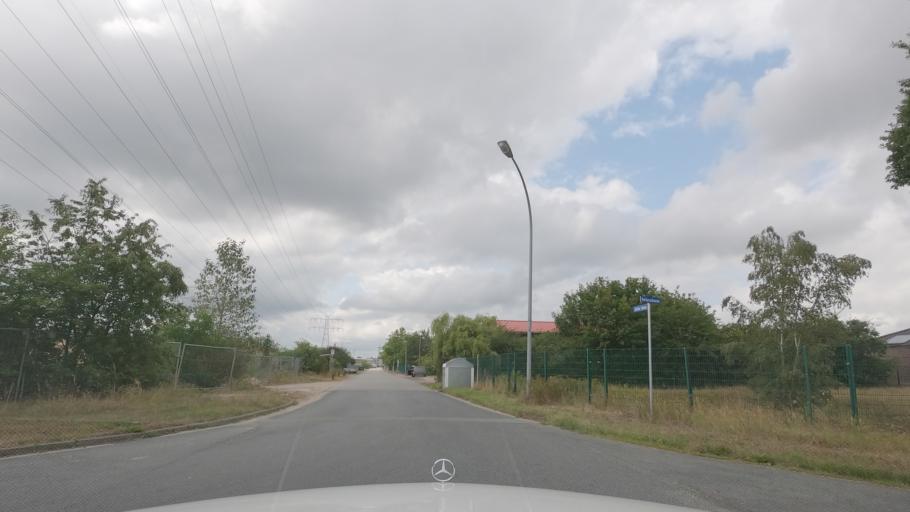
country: DE
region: Lower Saxony
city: Neuenkirchen
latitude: 53.2286
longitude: 8.5379
